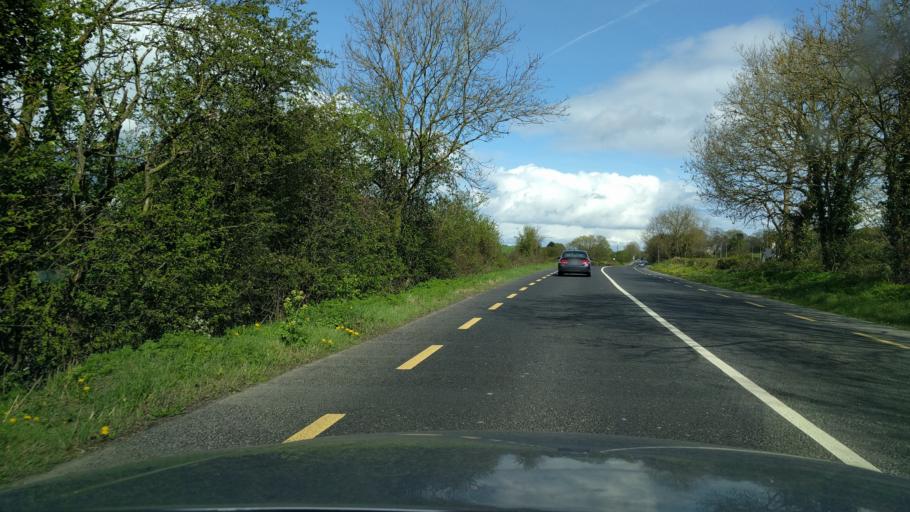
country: IE
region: Leinster
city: Balrothery
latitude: 53.5814
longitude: -6.1978
